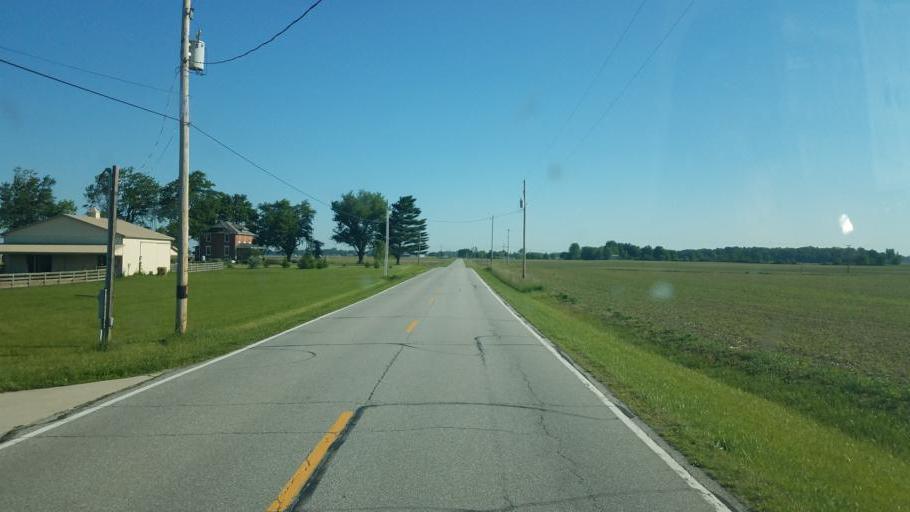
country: US
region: Ohio
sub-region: Crawford County
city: Bucyrus
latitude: 40.7598
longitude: -82.9538
